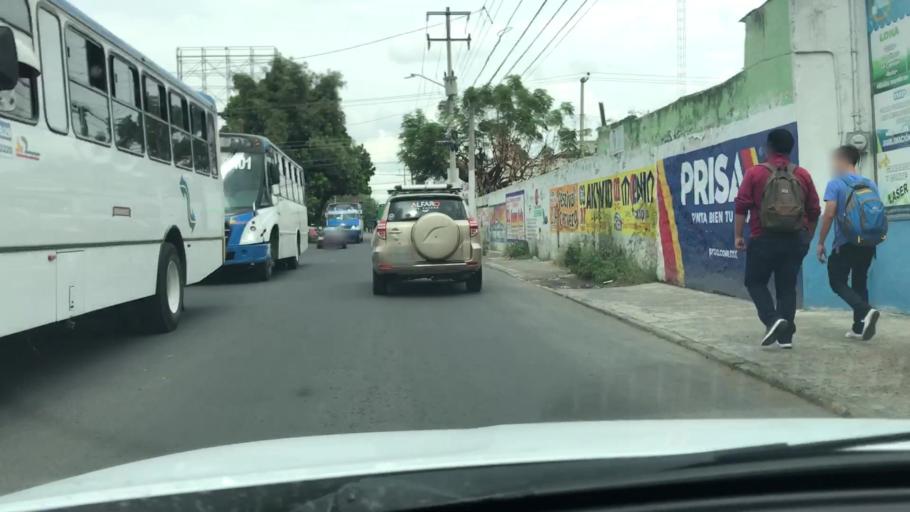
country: MX
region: Jalisco
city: Guadalajara
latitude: 20.6457
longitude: -103.4327
